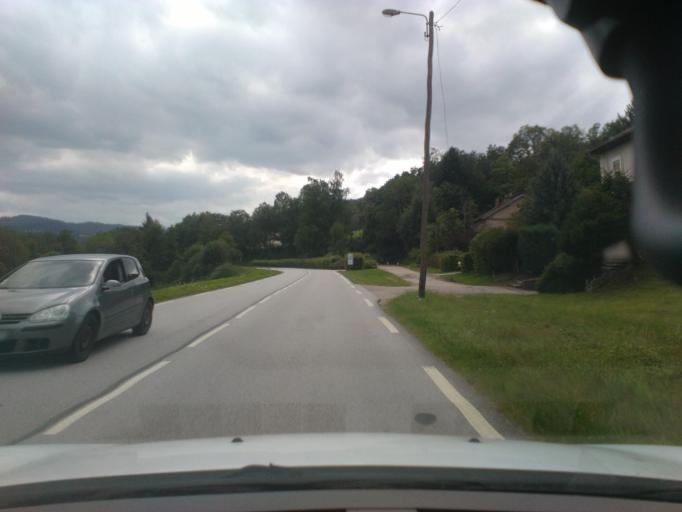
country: FR
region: Lorraine
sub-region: Departement des Vosges
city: Bruyeres
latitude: 48.1863
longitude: 6.6850
